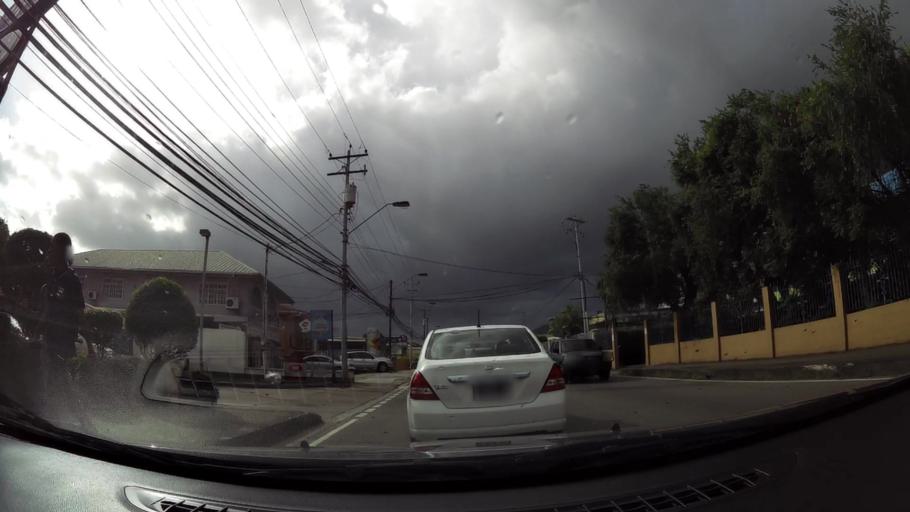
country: TT
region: Tunapuna/Piarco
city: Tunapuna
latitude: 10.6455
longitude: -61.3970
